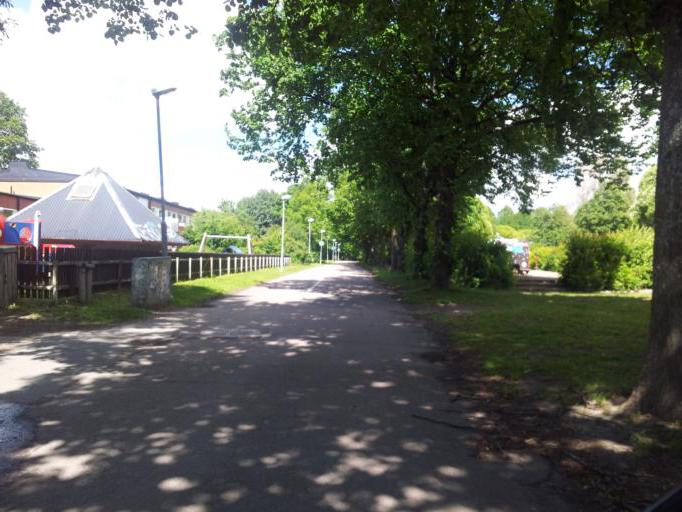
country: SE
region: Uppsala
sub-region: Uppsala Kommun
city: Uppsala
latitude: 59.8689
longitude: 17.6513
